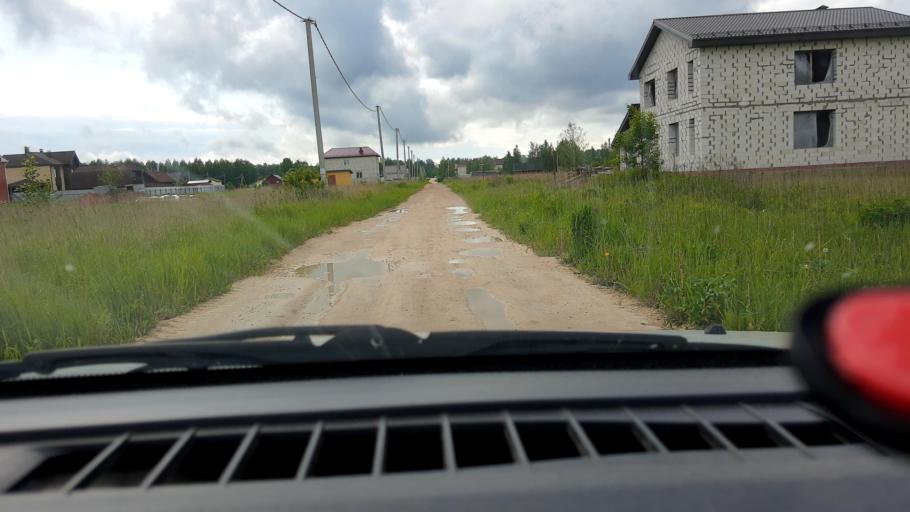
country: RU
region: Nizjnij Novgorod
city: Neklyudovo
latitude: 56.4303
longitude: 43.9716
